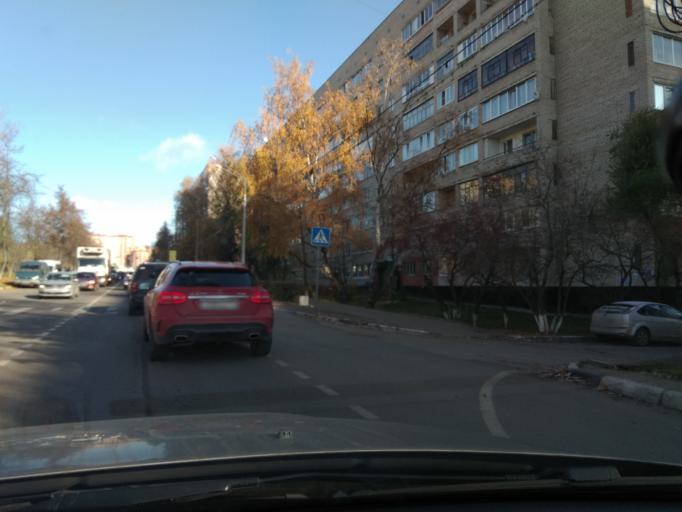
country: RU
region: Moskovskaya
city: Istra
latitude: 55.9052
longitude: 36.8591
